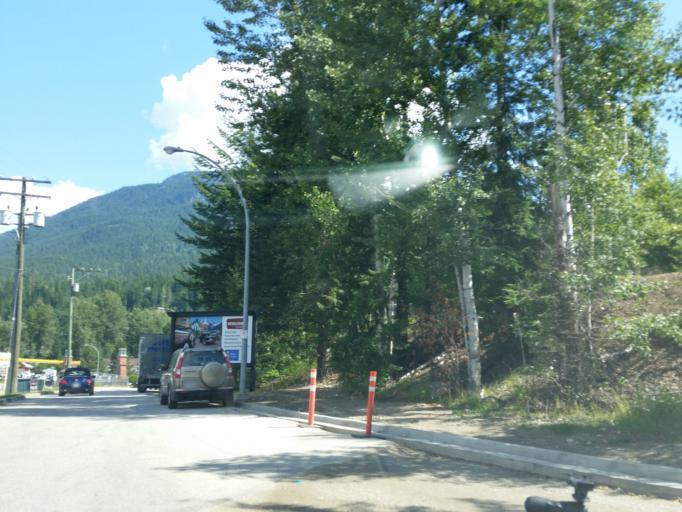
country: CA
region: British Columbia
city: Revelstoke
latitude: 51.0074
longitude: -118.2168
